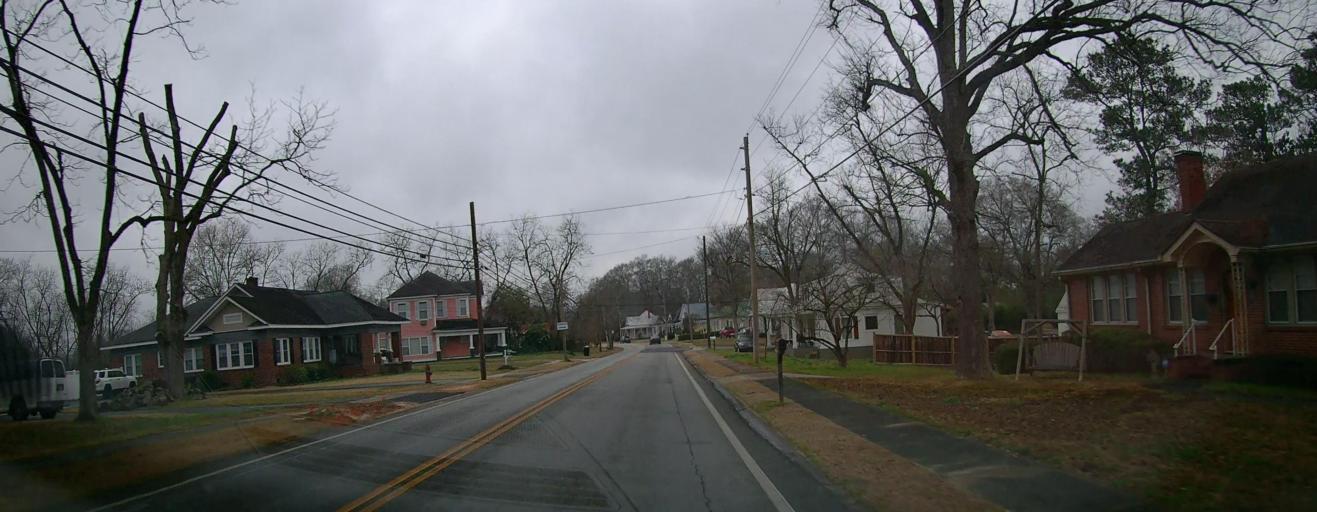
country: US
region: Georgia
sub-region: Lamar County
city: Barnesville
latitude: 33.0542
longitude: -84.1449
